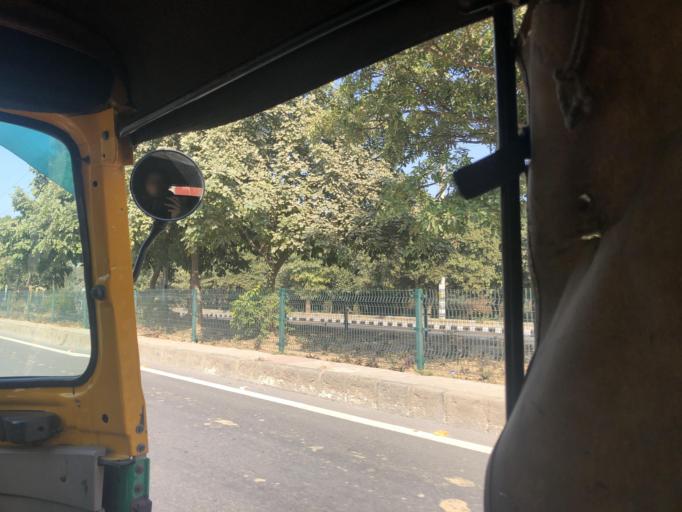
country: IN
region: Haryana
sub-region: Gurgaon
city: Gurgaon
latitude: 28.4408
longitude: 77.0869
